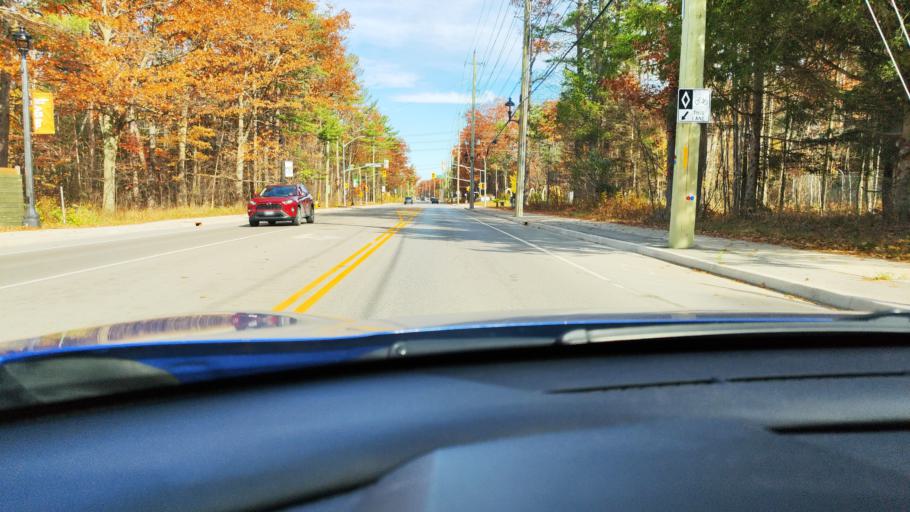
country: CA
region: Ontario
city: Wasaga Beach
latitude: 44.5000
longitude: -80.0378
